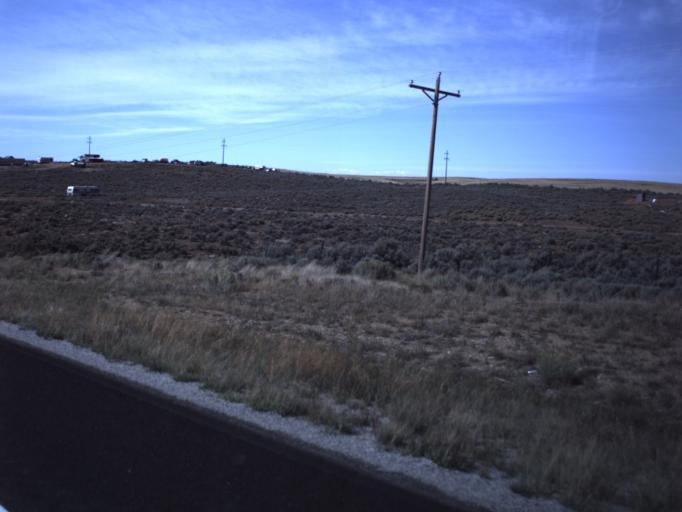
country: US
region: Utah
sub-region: San Juan County
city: Monticello
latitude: 37.8696
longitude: -109.2493
